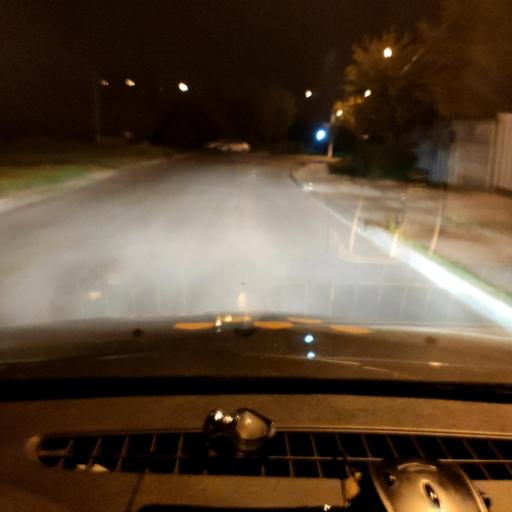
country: RU
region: Belgorod
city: Mayskiy
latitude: 50.5176
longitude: 36.4625
